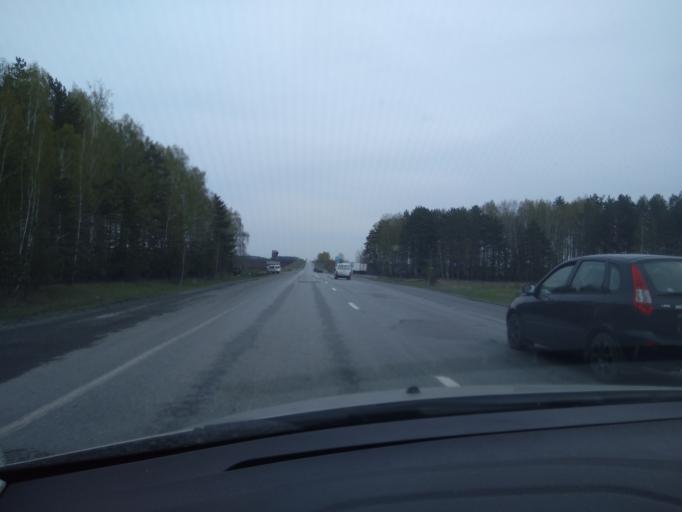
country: RU
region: Sverdlovsk
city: Gryaznovskoye
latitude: 56.7793
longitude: 61.5869
